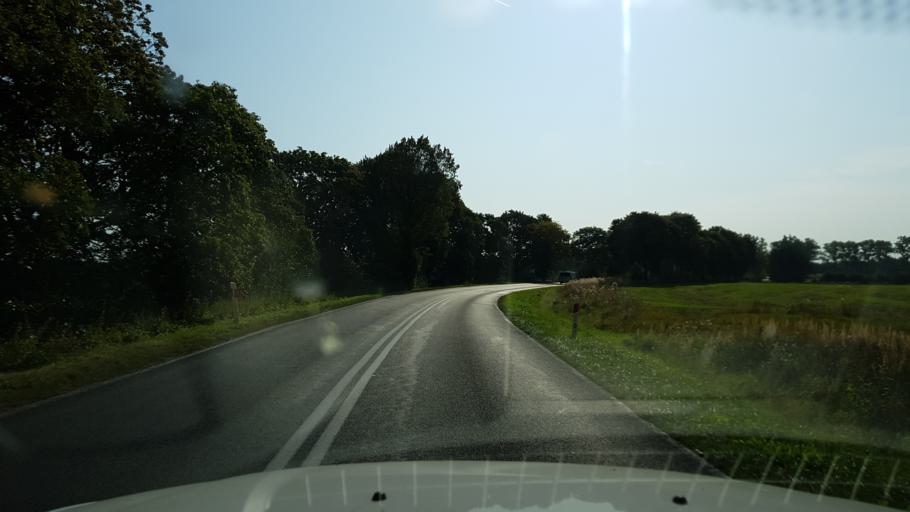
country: PL
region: West Pomeranian Voivodeship
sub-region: Powiat lobeski
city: Resko
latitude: 53.7788
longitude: 15.3604
